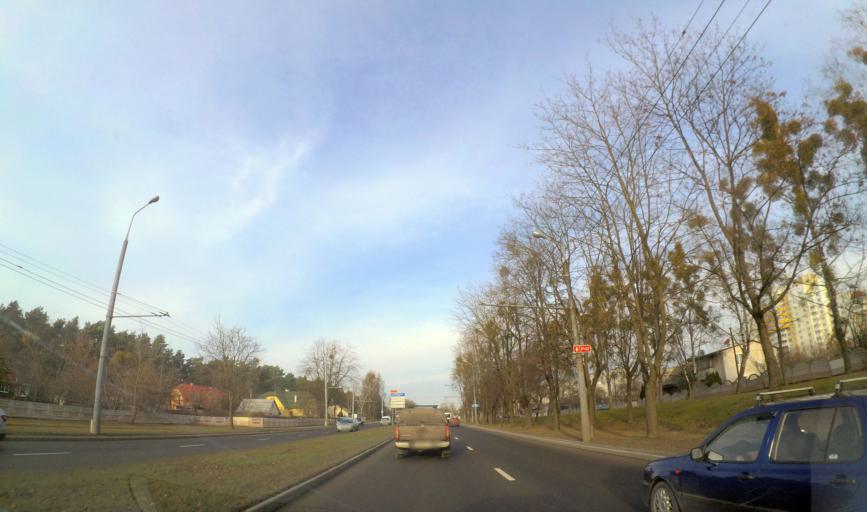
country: BY
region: Grodnenskaya
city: Hrodna
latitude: 53.6880
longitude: 23.8007
